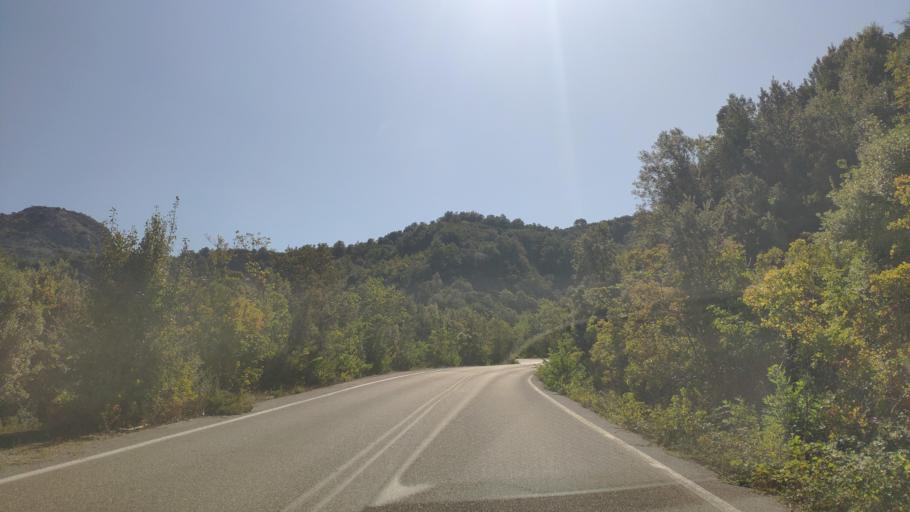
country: GR
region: West Greece
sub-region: Nomos Aitolias kai Akarnanias
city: Sardinia
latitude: 38.9214
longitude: 21.3981
